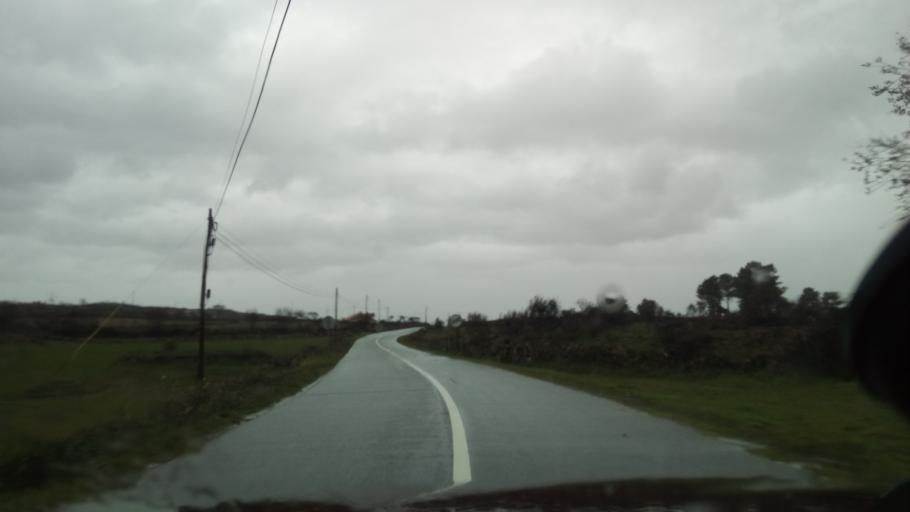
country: PT
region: Guarda
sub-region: Fornos de Algodres
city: Fornos de Algodres
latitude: 40.5619
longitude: -7.5173
